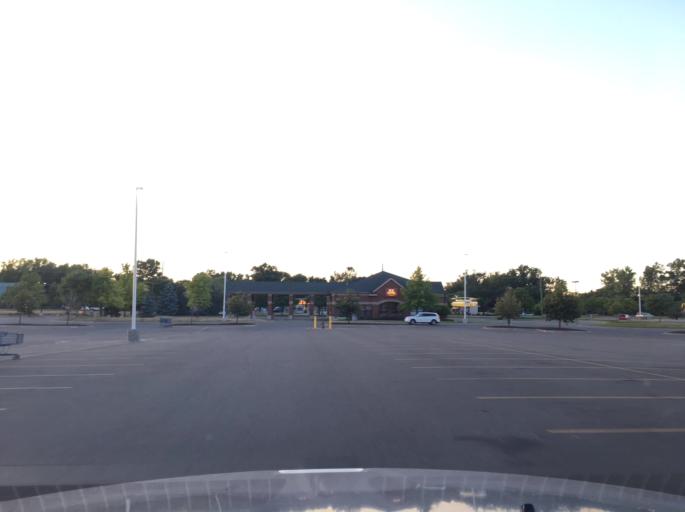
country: US
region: Michigan
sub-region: Macomb County
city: Fraser
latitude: 42.5519
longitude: -82.9629
